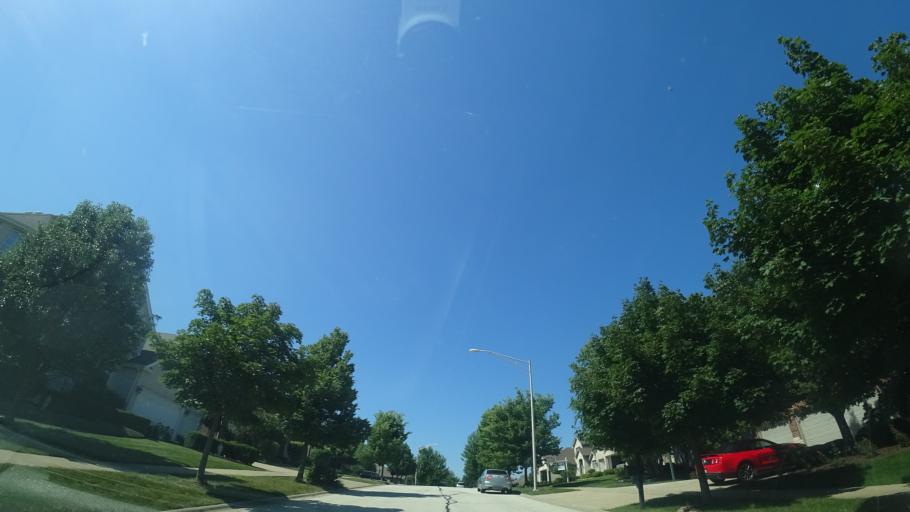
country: US
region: Illinois
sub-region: Will County
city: Mokena
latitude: 41.5692
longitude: -87.8990
